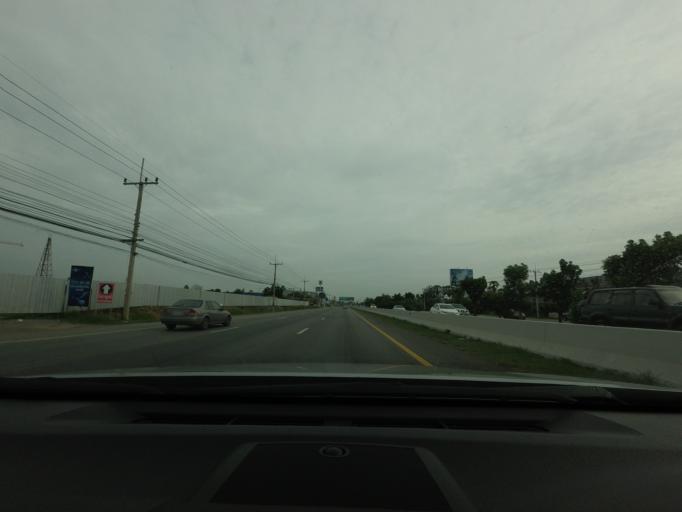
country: TH
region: Phetchaburi
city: Ban Lat
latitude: 13.0635
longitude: 99.9456
